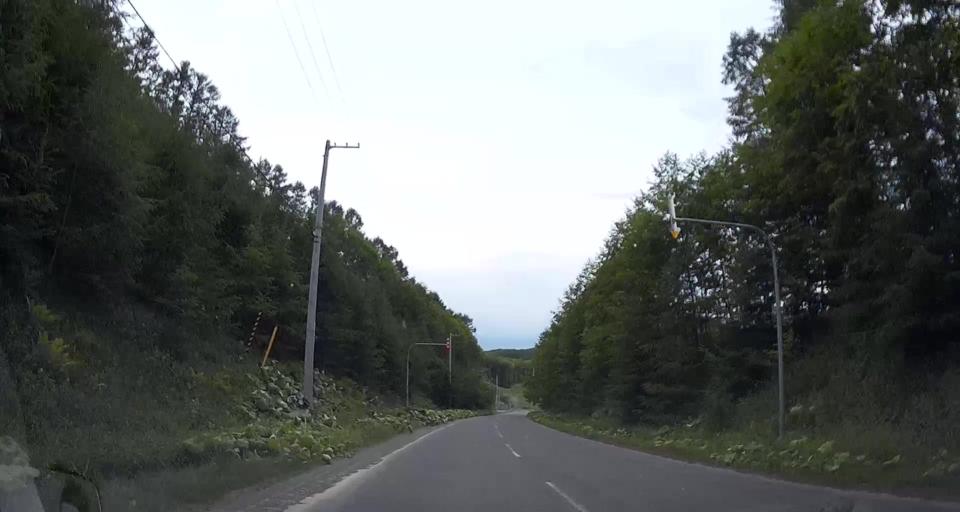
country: JP
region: Hokkaido
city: Chitose
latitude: 42.7634
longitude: 141.9928
